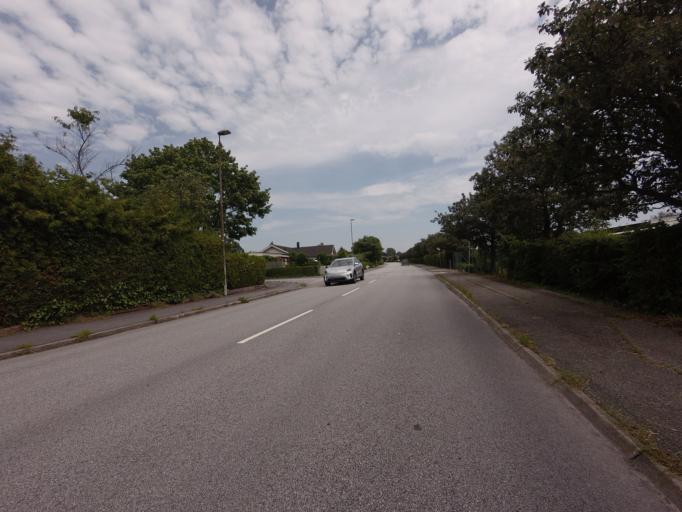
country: SE
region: Skane
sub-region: Ystads Kommun
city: Ystad
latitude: 55.4270
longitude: 13.7939
